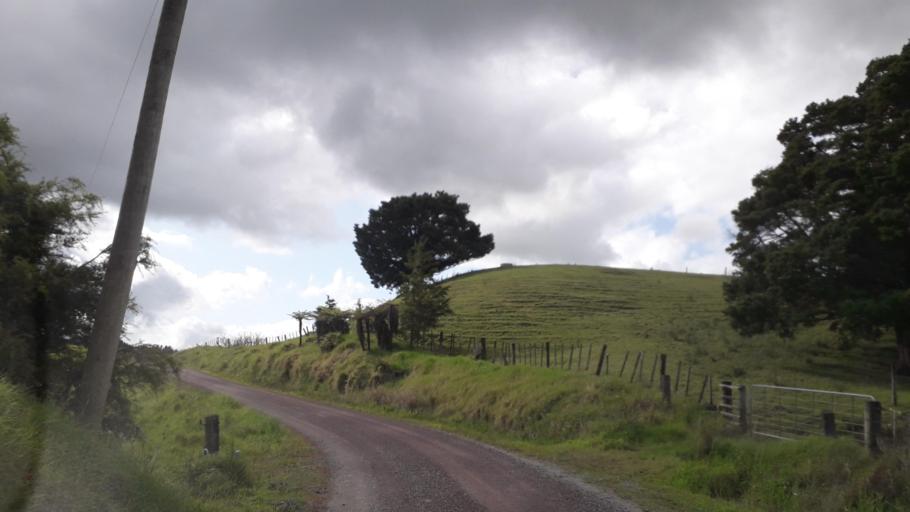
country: NZ
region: Northland
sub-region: Far North District
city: Waimate North
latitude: -35.3127
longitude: 173.5654
